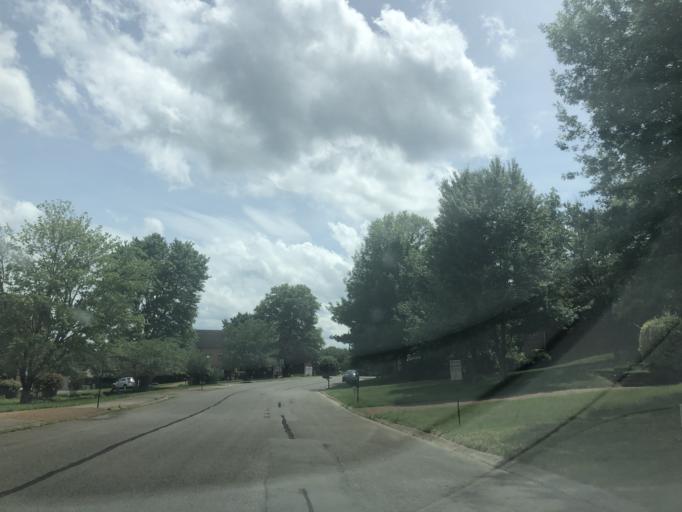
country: US
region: Tennessee
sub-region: Davidson County
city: Belle Meade
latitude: 36.0565
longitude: -86.9526
